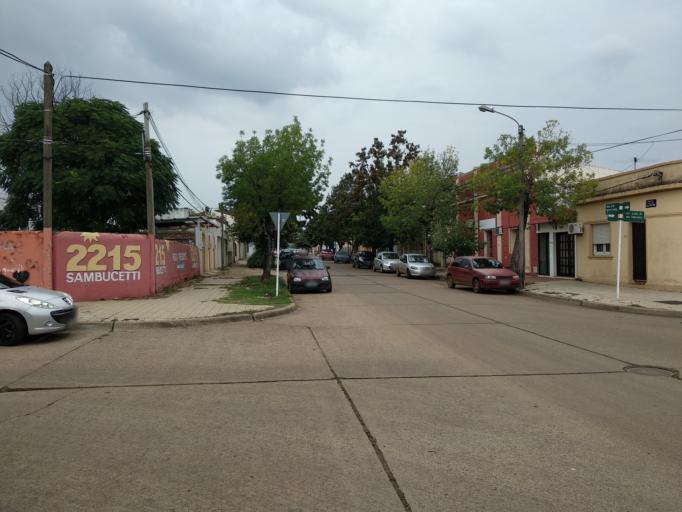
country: UY
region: Artigas
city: Artigas
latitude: -30.4012
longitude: -56.4688
